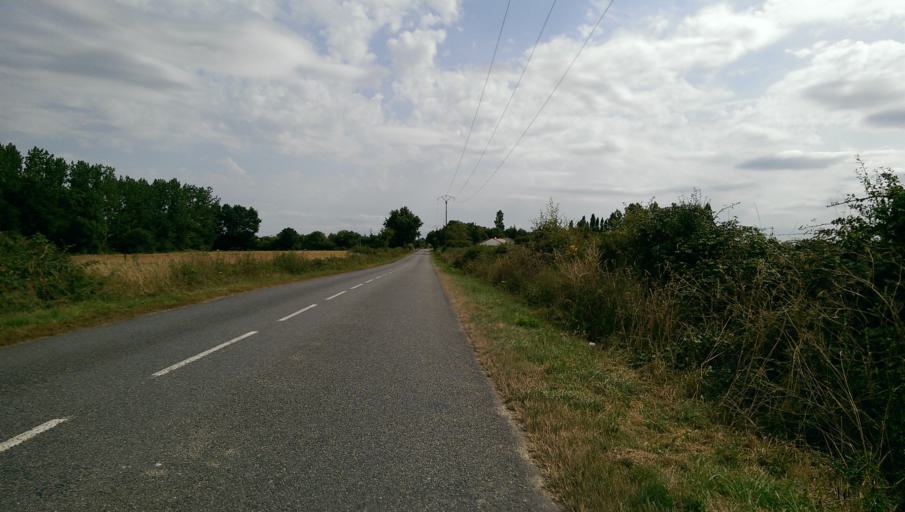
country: FR
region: Pays de la Loire
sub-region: Departement de la Loire-Atlantique
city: Vieillevigne
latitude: 46.9939
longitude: -1.4285
